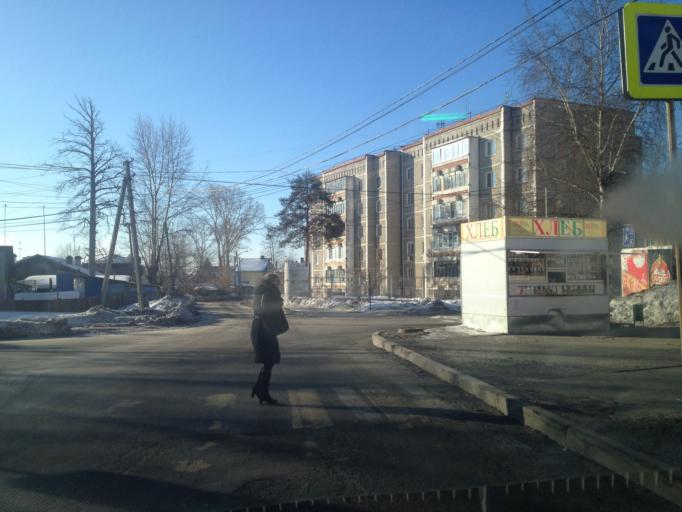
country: RU
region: Sverdlovsk
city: Sovkhoznyy
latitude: 56.7723
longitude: 60.5892
